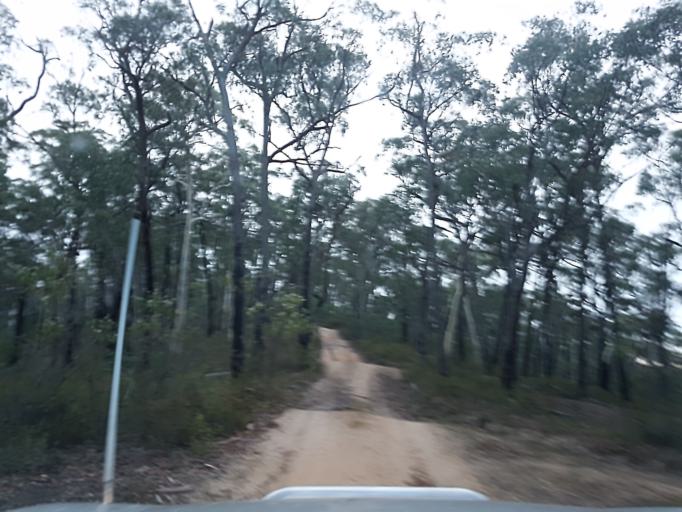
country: AU
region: New South Wales
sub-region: Snowy River
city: Jindabyne
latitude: -36.8631
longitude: 148.2368
